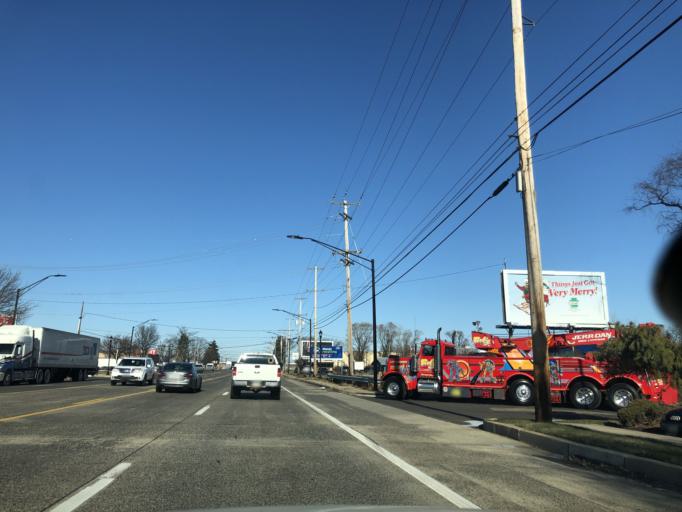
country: US
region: Pennsylvania
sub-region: Bucks County
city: Bristol
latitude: 40.1184
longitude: -74.8811
